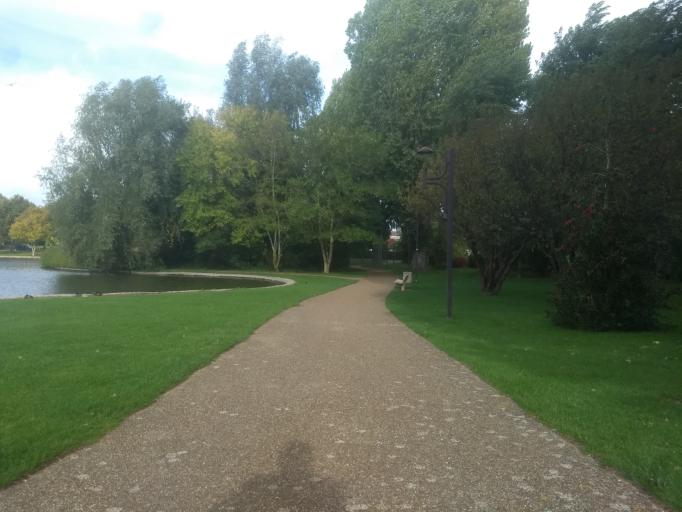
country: FR
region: Nord-Pas-de-Calais
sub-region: Departement du Pas-de-Calais
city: Dainville
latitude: 50.2829
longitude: 2.7357
